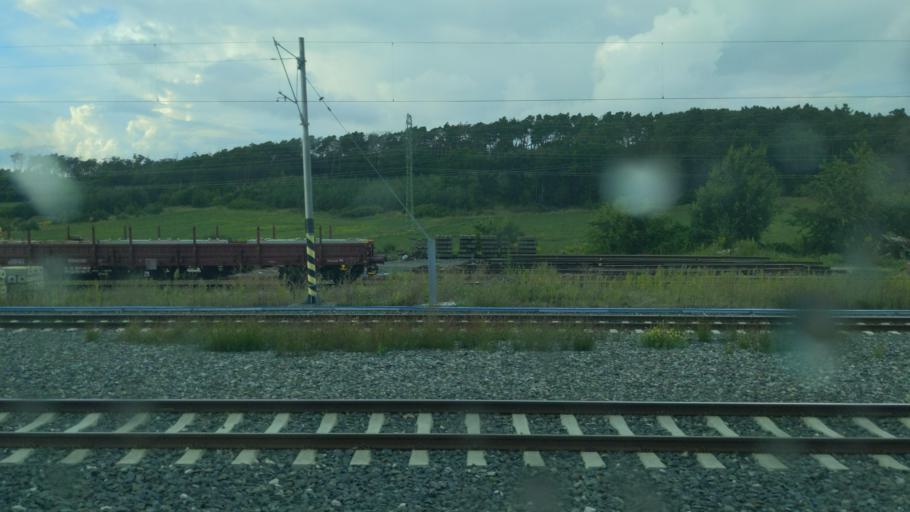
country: CZ
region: Central Bohemia
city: Poricany
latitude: 50.1117
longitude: 14.9267
